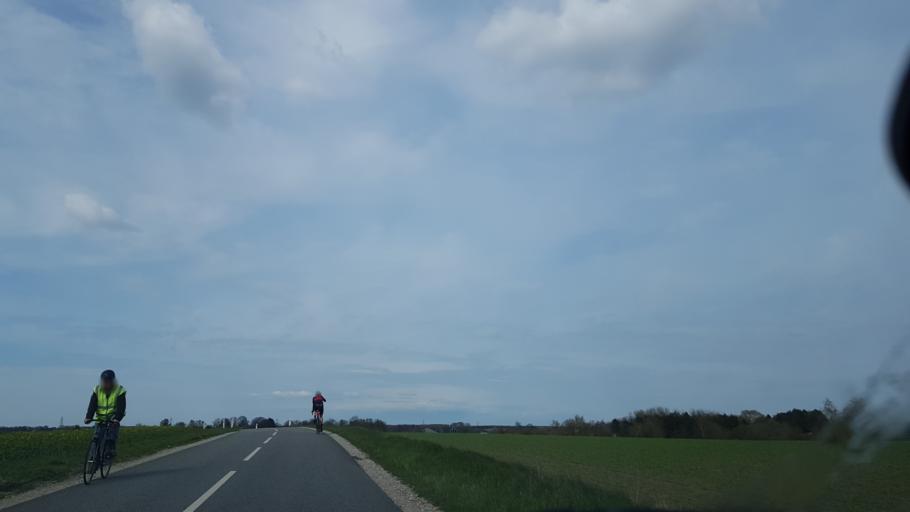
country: DK
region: Capital Region
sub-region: Allerod Kommune
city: Lynge
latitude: 55.8665
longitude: 12.2967
